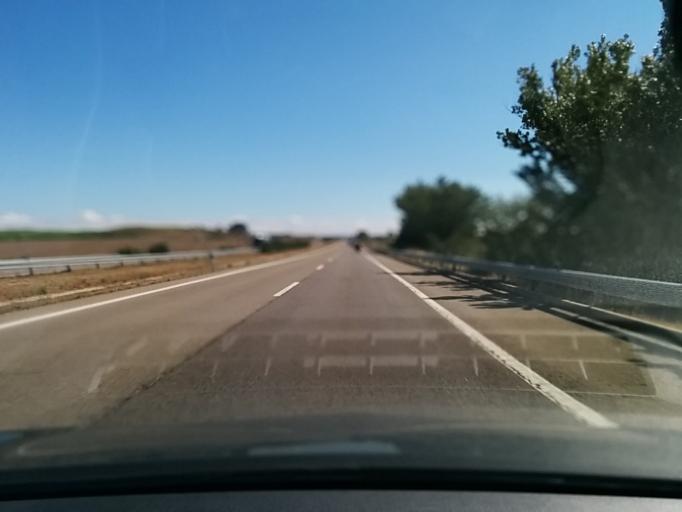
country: ES
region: Aragon
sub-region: Provincia de Huesca
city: Almudebar
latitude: 42.0167
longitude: -0.6162
